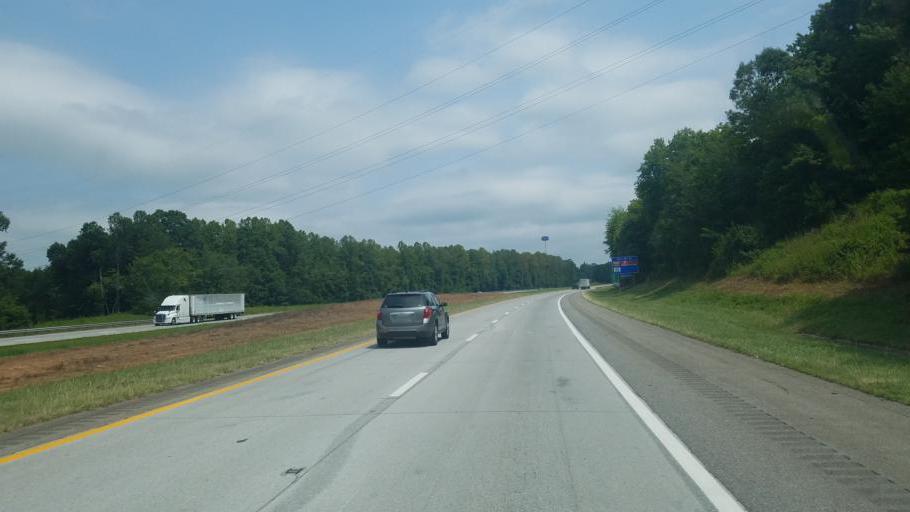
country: US
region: North Carolina
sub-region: Surry County
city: Elkin
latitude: 36.2722
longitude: -80.8251
